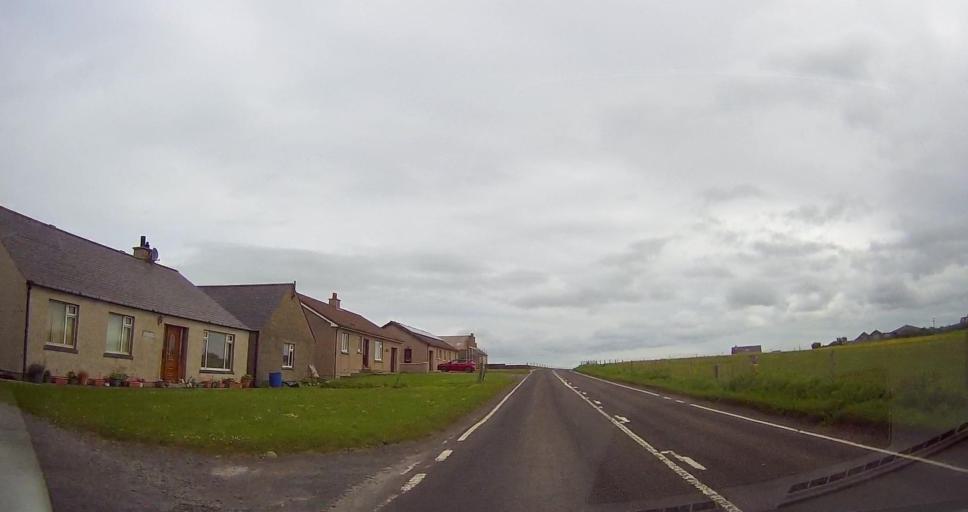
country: GB
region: Scotland
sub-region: Orkney Islands
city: Stromness
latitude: 58.9842
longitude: -3.2455
